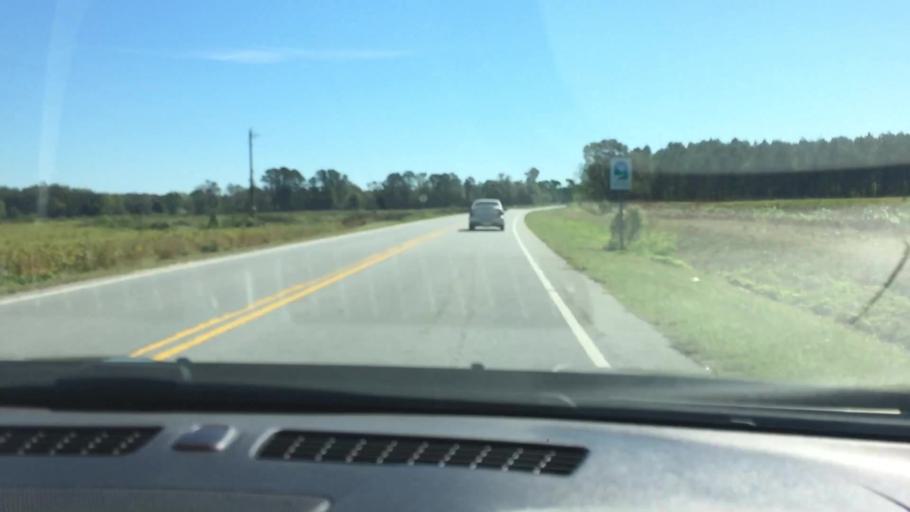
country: US
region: North Carolina
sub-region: Pitt County
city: Grifton
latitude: 35.3498
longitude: -77.3272
